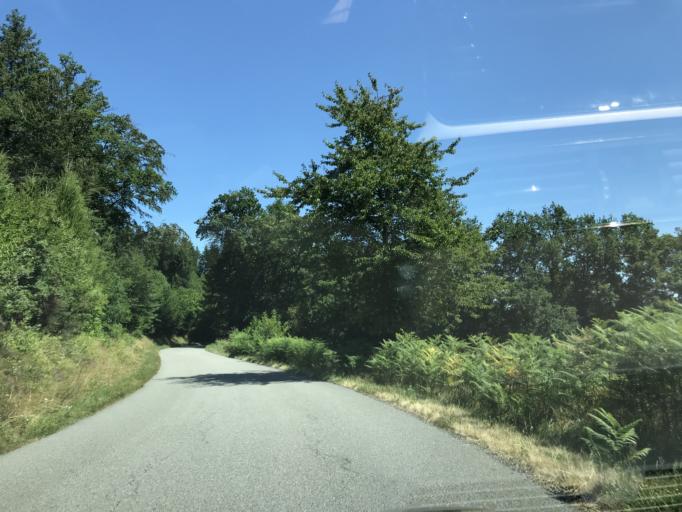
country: FR
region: Limousin
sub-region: Departement de la Correze
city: Neuvic
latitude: 45.3753
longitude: 2.2611
